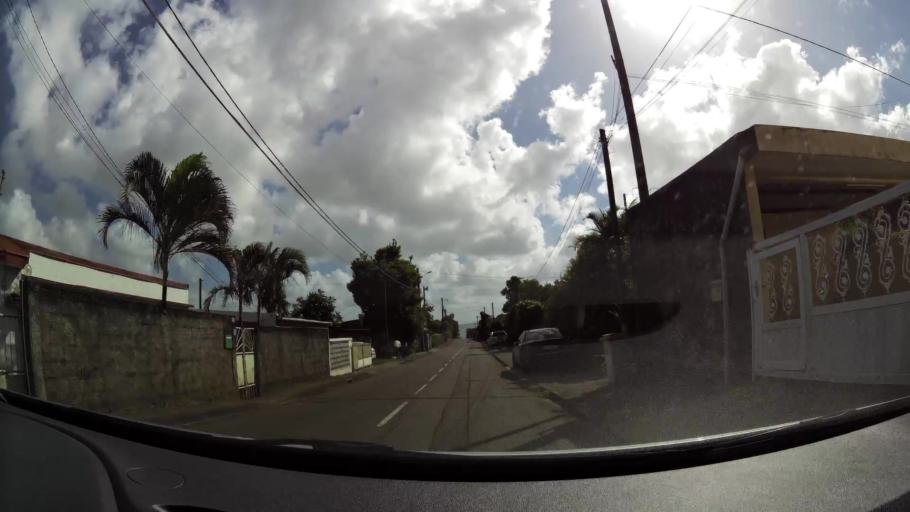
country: MQ
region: Martinique
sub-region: Martinique
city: Fort-de-France
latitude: 14.6373
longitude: -61.0596
